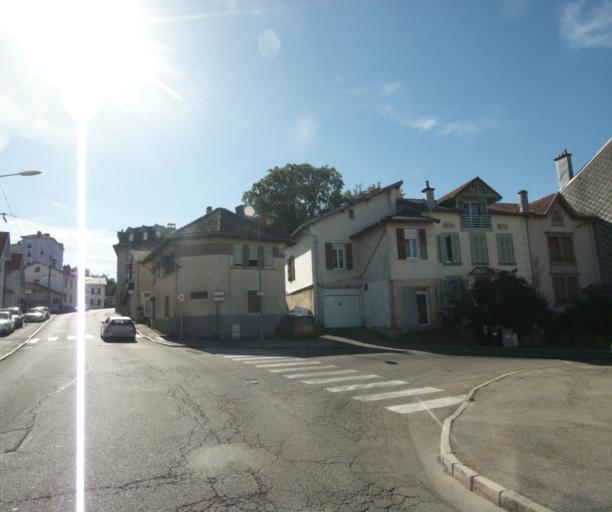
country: FR
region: Lorraine
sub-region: Departement des Vosges
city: Chantraine
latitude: 48.1724
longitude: 6.4422
